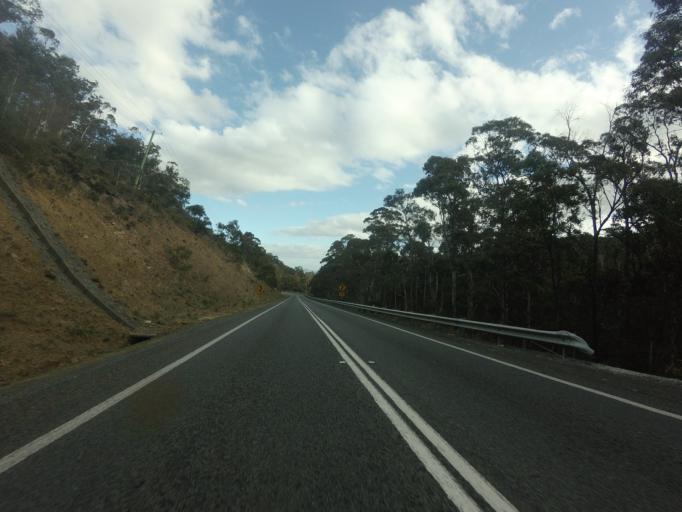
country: AU
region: Tasmania
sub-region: Sorell
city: Sorell
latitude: -42.6674
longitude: 147.5281
